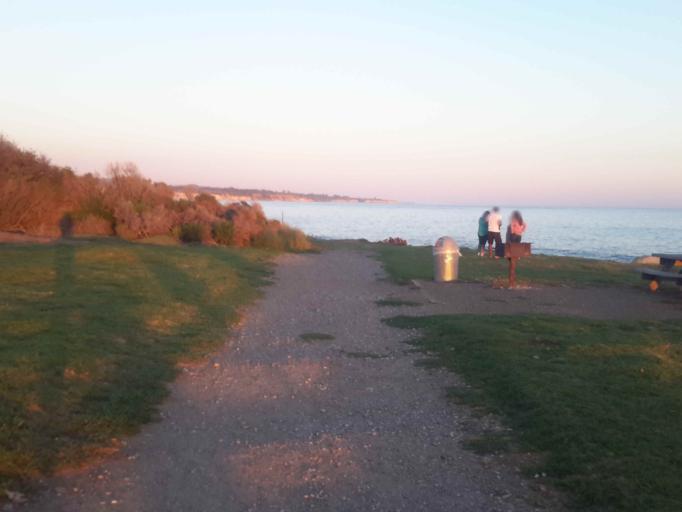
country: US
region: California
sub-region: Santa Barbara County
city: Santa Ynez
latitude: 34.4580
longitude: -120.0231
